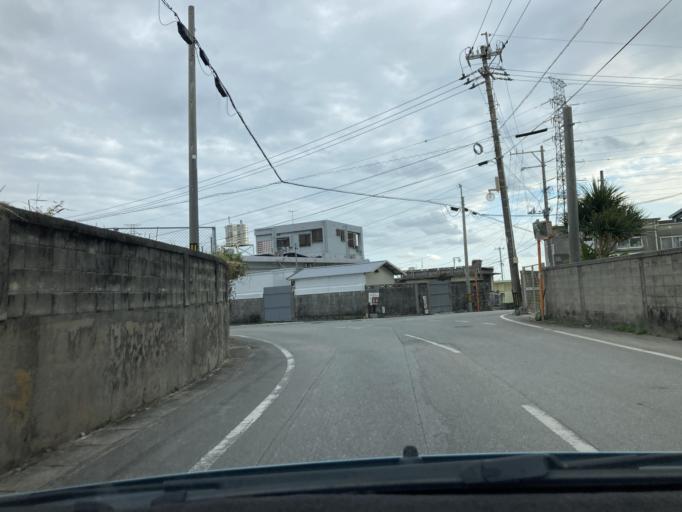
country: JP
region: Okinawa
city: Ishikawa
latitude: 26.4499
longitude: 127.9135
